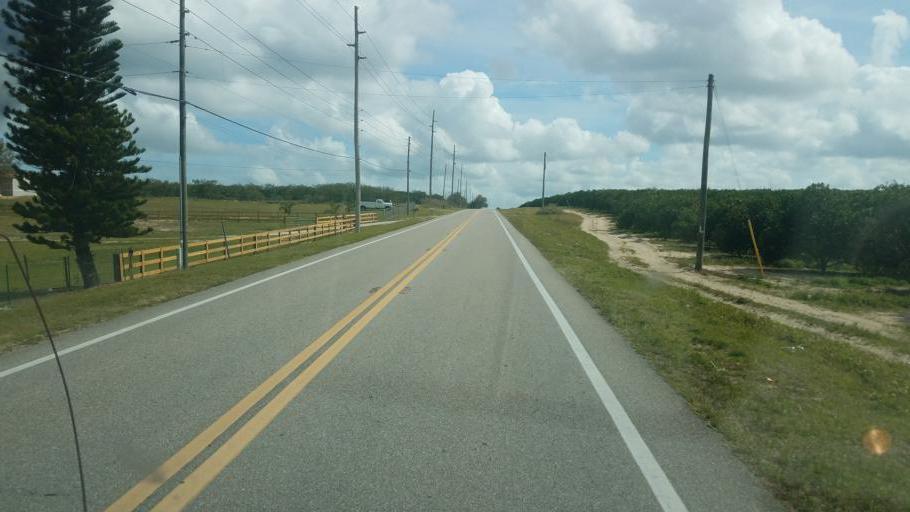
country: US
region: Florida
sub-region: Polk County
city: Dundee
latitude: 28.0409
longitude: -81.5748
